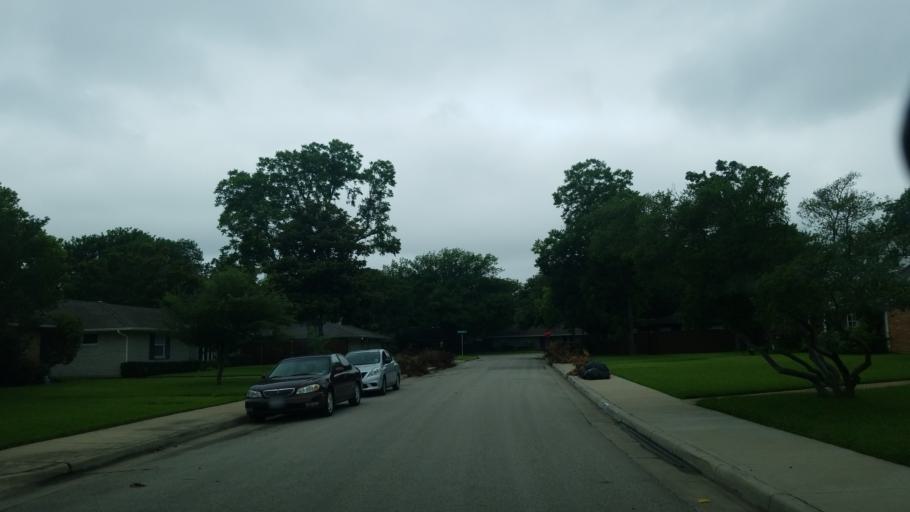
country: US
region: Texas
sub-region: Dallas County
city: Farmers Branch
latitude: 32.8931
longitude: -96.8687
